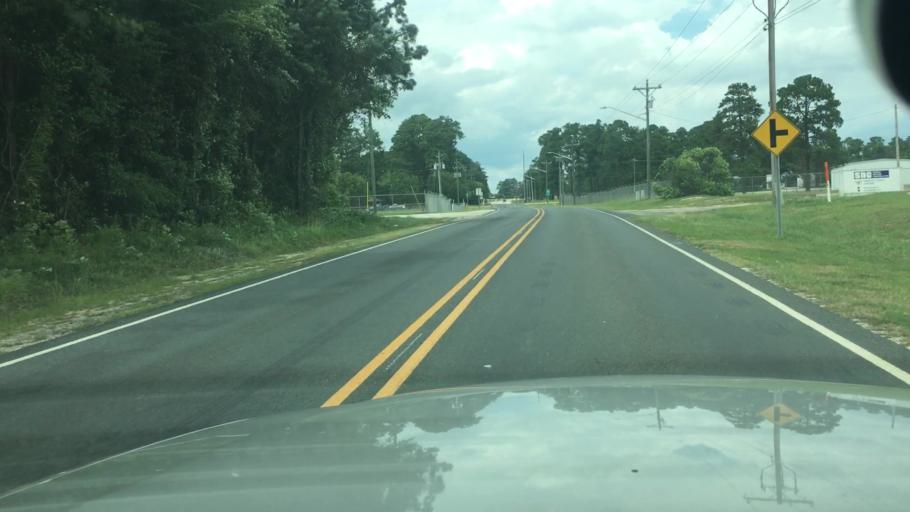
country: US
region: North Carolina
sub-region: Cumberland County
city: Hope Mills
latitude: 34.9897
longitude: -78.8906
